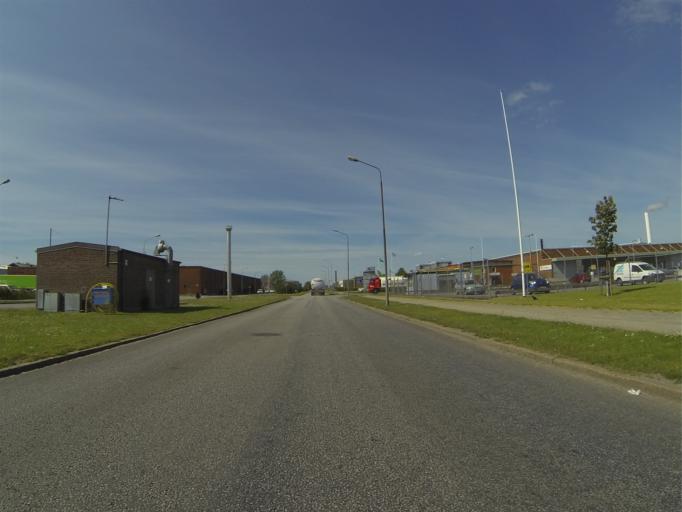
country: SE
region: Skane
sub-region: Burlovs Kommun
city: Arloev
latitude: 55.6260
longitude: 13.0373
